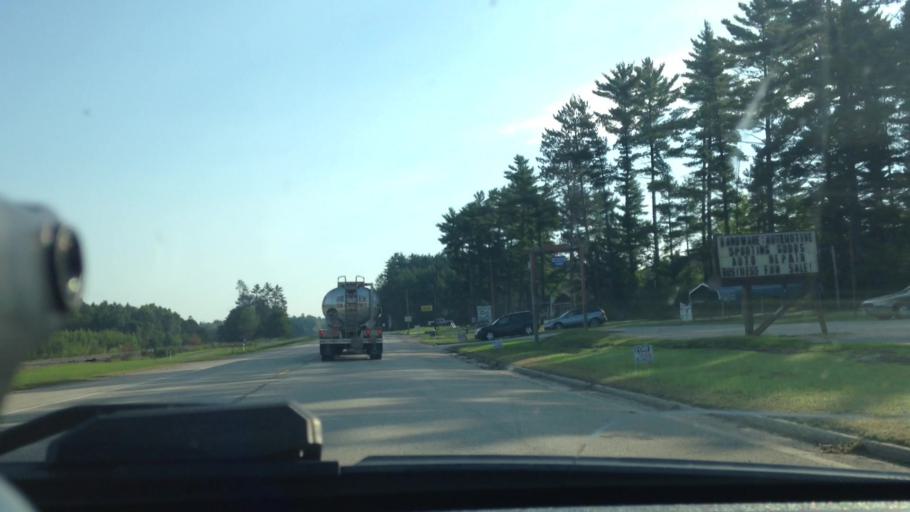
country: US
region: Wisconsin
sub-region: Marinette County
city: Niagara
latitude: 45.6364
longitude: -87.9881
